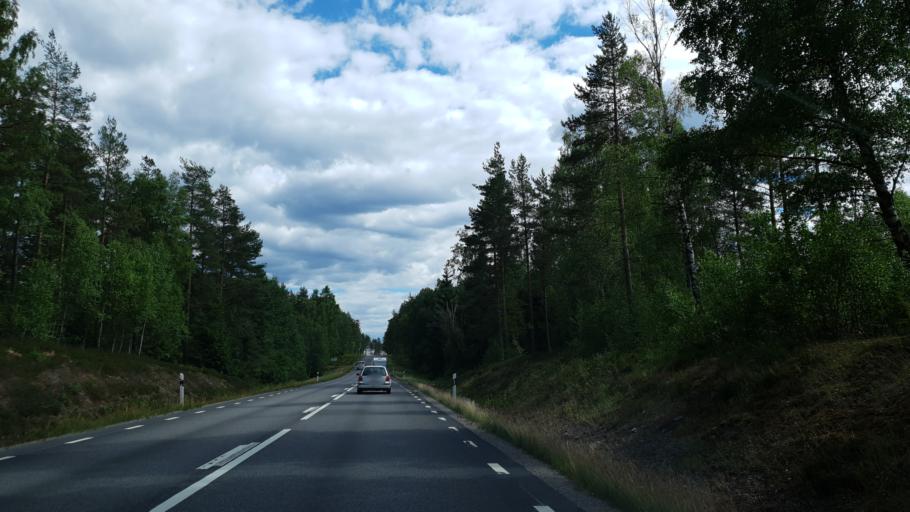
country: SE
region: Kronoberg
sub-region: Lessebo Kommun
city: Lessebo
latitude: 56.8233
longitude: 15.4055
